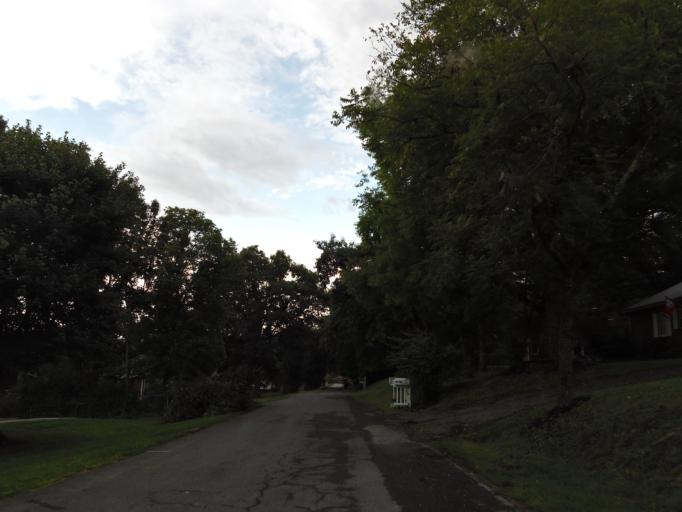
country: US
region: Tennessee
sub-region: Blount County
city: Eagleton Village
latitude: 35.8002
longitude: -83.9482
